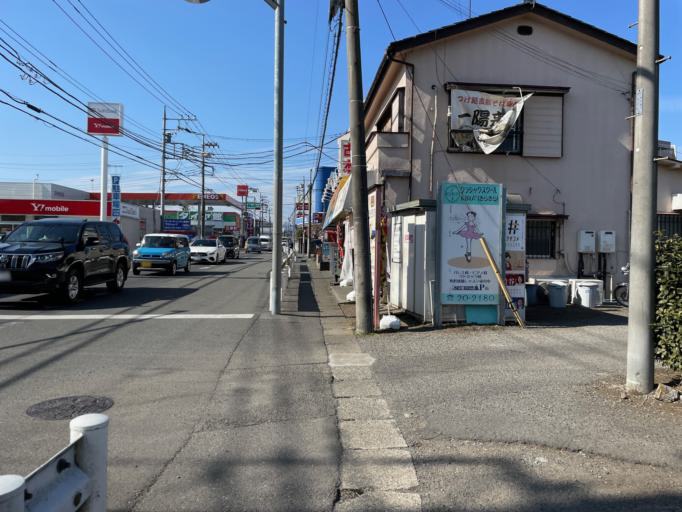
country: JP
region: Tokyo
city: Hachioji
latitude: 35.6803
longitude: 139.3076
